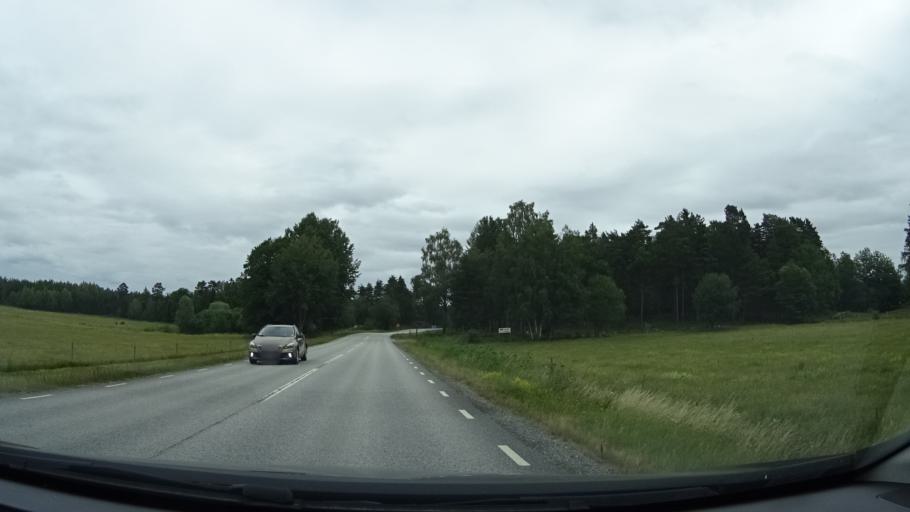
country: SE
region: Stockholm
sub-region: Varmdo Kommun
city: Hemmesta
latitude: 59.3549
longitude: 18.4835
